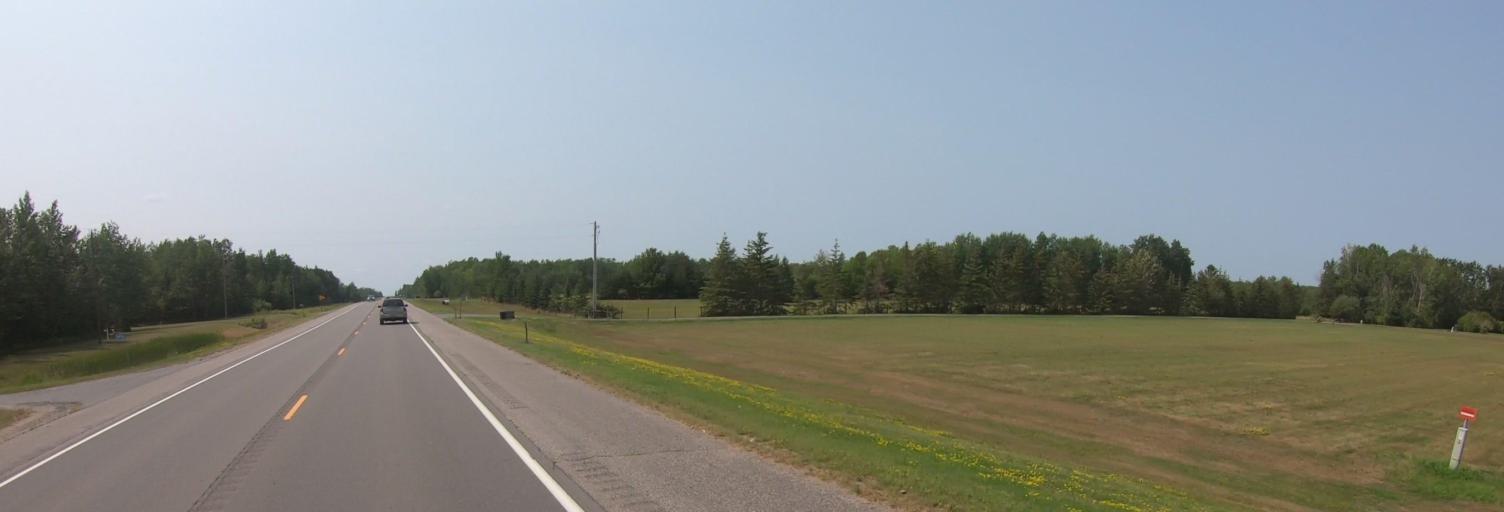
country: US
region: Minnesota
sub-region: Koochiching County
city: International Falls
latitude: 48.5450
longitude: -93.4610
